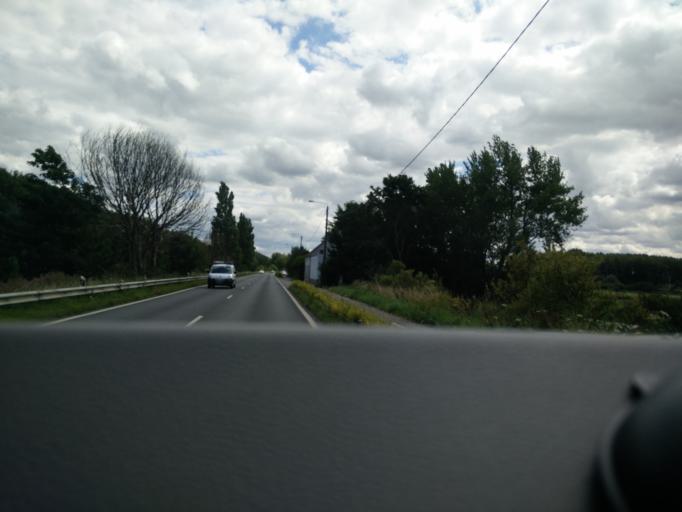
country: FR
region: Nord-Pas-de-Calais
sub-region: Departement du Nord
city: Bergues
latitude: 50.9771
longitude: 2.4185
